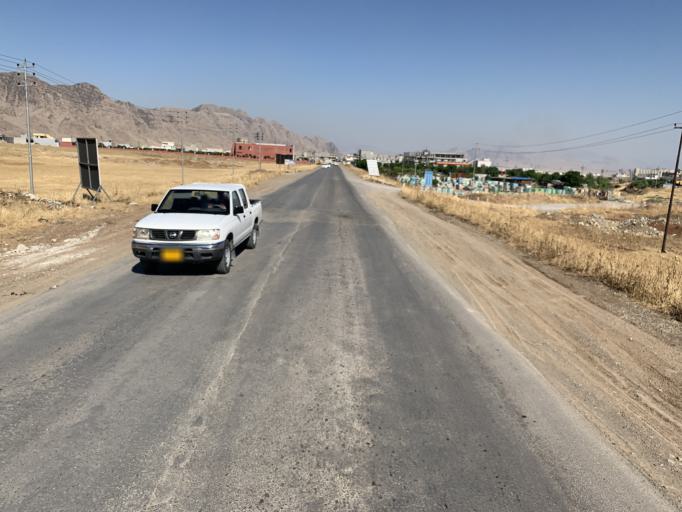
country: IQ
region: As Sulaymaniyah
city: Raniye
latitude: 36.2623
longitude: 44.8516
